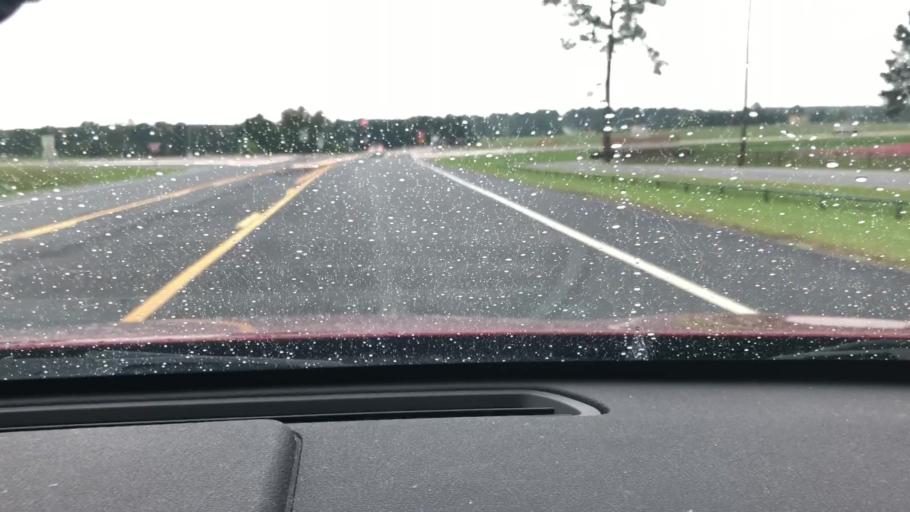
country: US
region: Arkansas
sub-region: Columbia County
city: Magnolia
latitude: 33.2960
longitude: -93.2361
